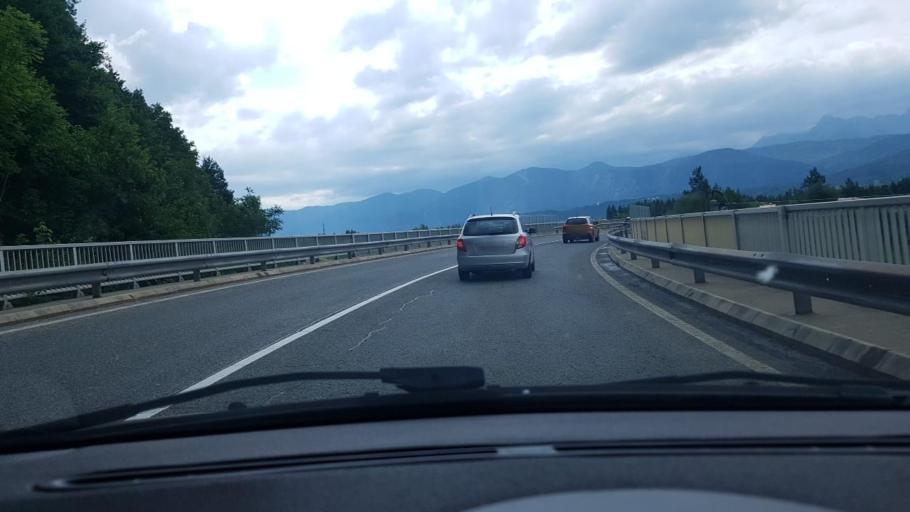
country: AT
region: Carinthia
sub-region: Politischer Bezirk Villach Land
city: Feistritz an der Gail
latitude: 46.5932
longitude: 13.6134
